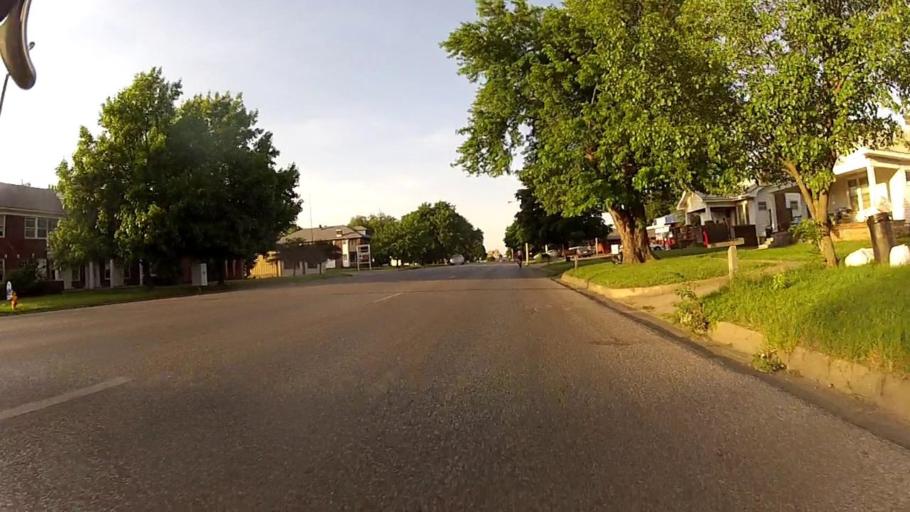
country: US
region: Kansas
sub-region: Cowley County
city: Arkansas City
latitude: 37.0730
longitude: -97.0392
